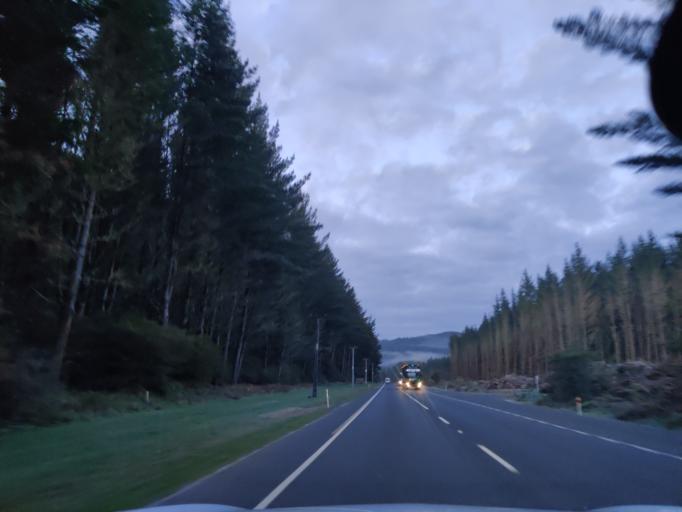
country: NZ
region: Waikato
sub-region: South Waikato District
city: Tokoroa
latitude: -38.3683
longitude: 176.0021
